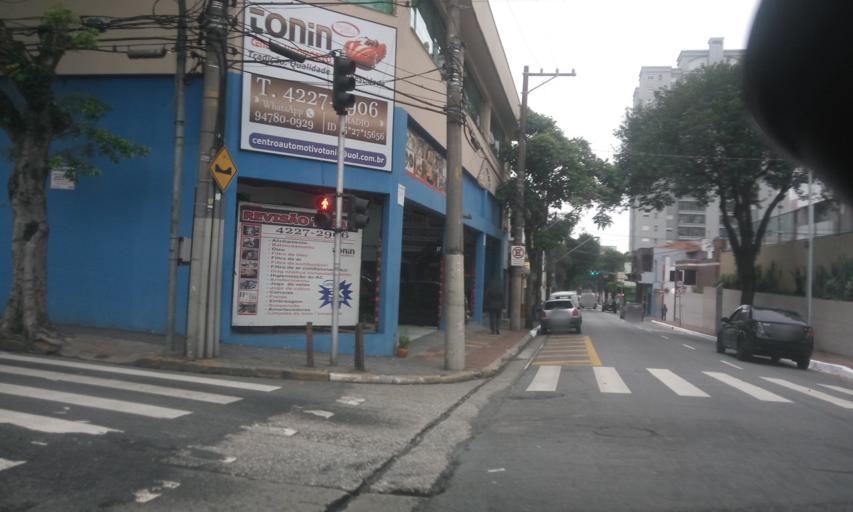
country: BR
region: Sao Paulo
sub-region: Sao Caetano Do Sul
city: Sao Caetano do Sul
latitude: -23.6221
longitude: -46.5695
